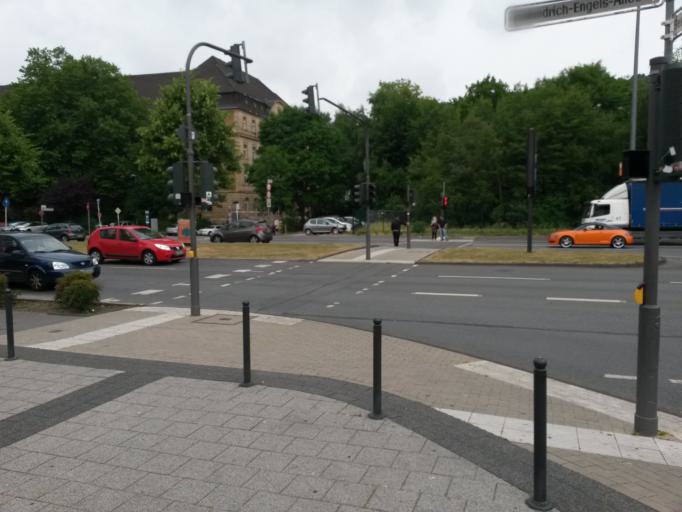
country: DE
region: North Rhine-Westphalia
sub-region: Regierungsbezirk Dusseldorf
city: Wuppertal
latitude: 51.2569
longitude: 7.1637
